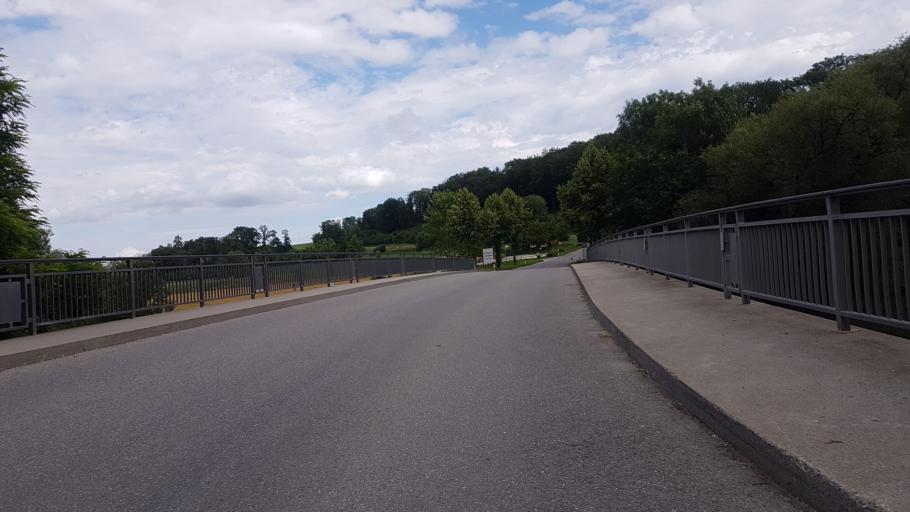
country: DE
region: Baden-Wuerttemberg
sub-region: Tuebingen Region
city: Emeringen
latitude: 48.2148
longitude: 9.5178
